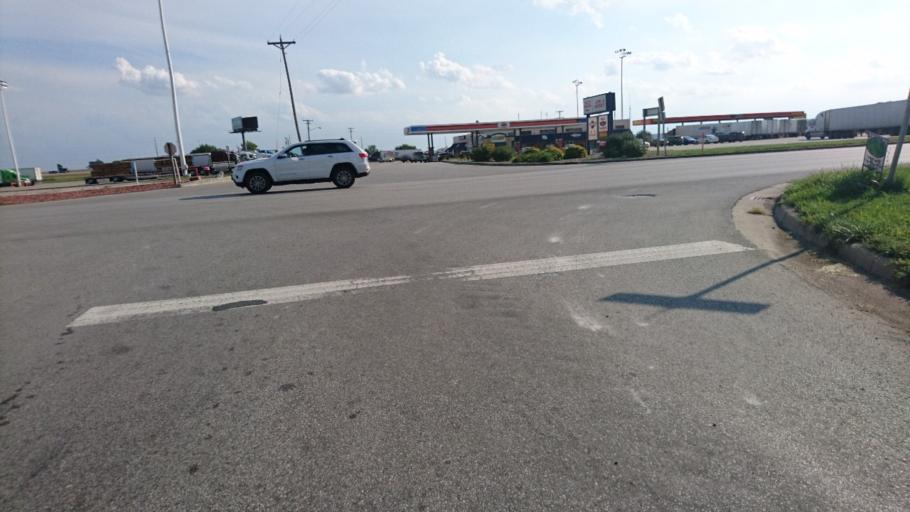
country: US
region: Illinois
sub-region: Logan County
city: Atlanta
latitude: 40.3118
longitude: -89.1683
